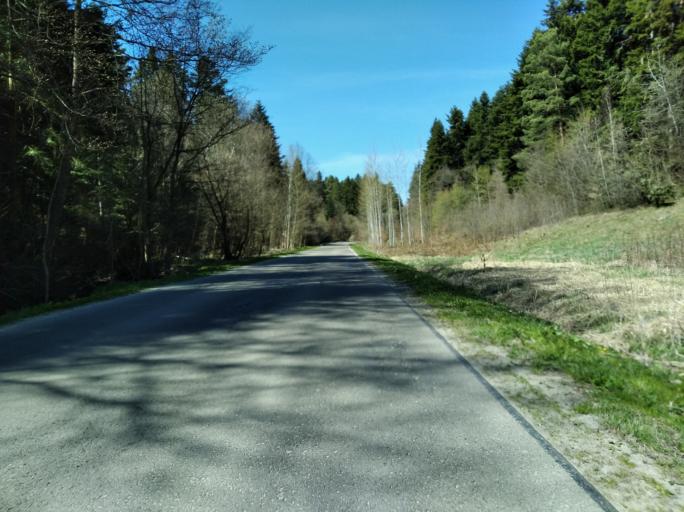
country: PL
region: Subcarpathian Voivodeship
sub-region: Powiat brzozowski
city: Golcowa
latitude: 49.7498
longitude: 22.0702
